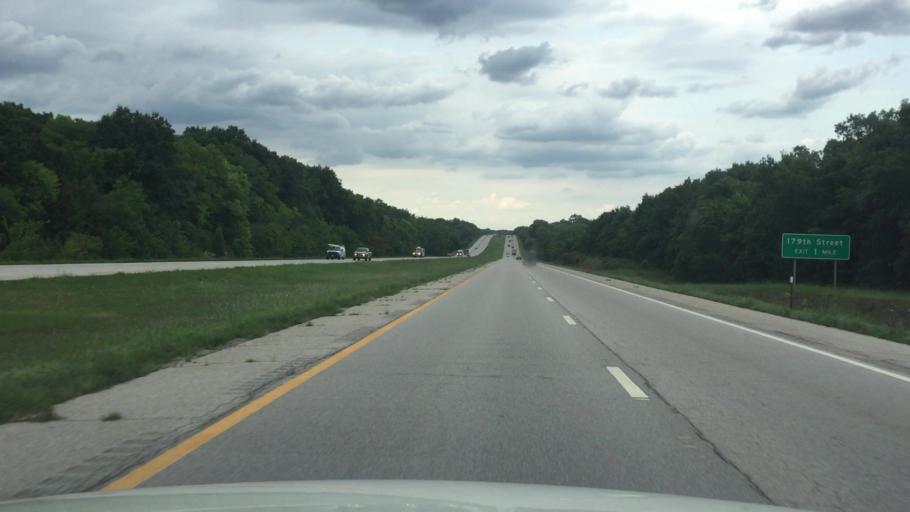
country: US
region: Missouri
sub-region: Cass County
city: Belton
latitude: 38.7866
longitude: -94.6770
